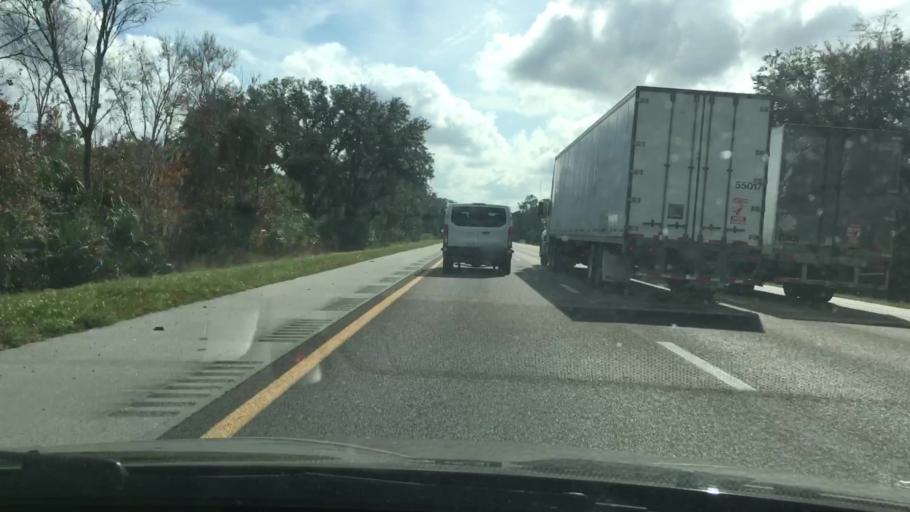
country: US
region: Florida
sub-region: Volusia County
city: Oak Hill
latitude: 28.8634
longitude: -80.9186
